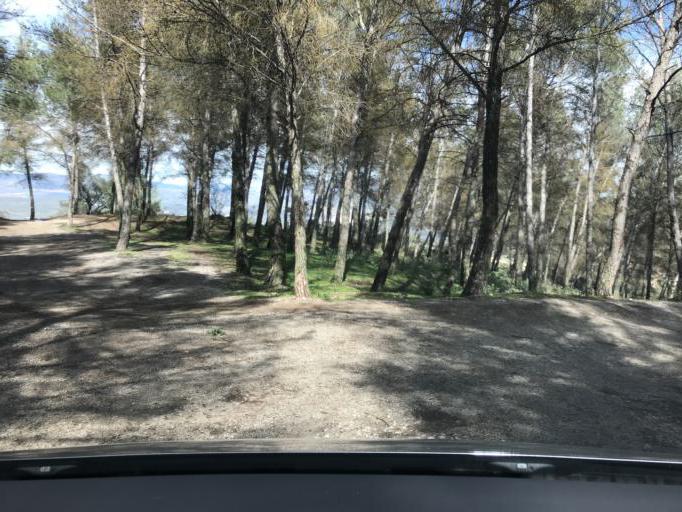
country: ES
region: Andalusia
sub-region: Provincia de Granada
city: Atarfe
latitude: 37.2434
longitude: -3.6894
